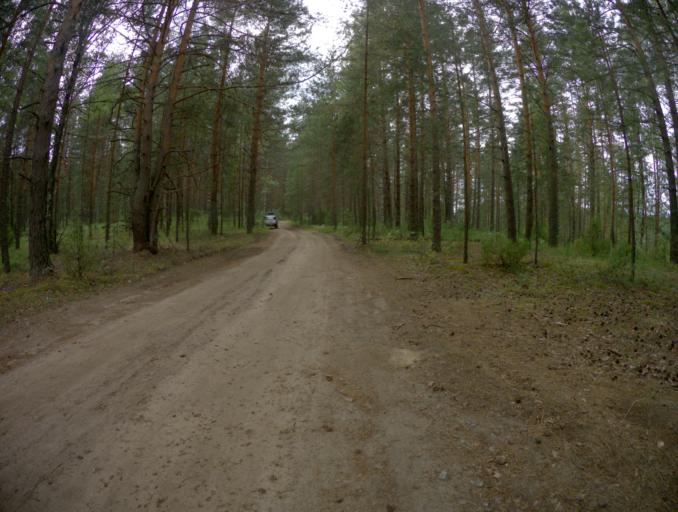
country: RU
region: Nizjnij Novgorod
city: Frolishchi
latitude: 56.3511
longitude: 42.7611
